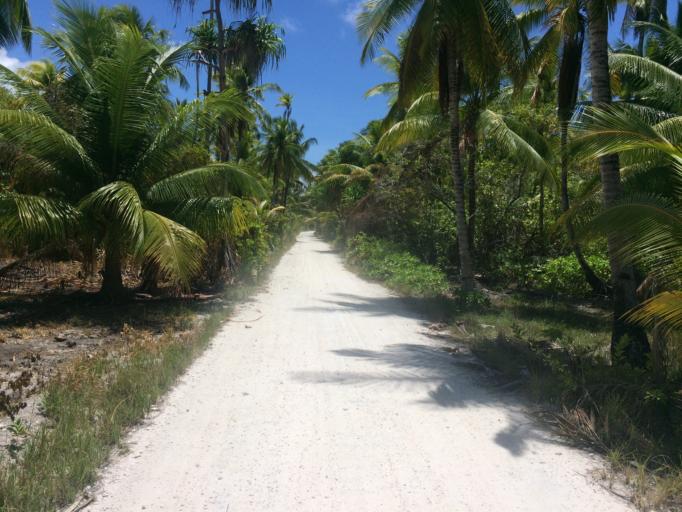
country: KI
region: Gilbert Islands
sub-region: Marakei
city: Rawannawi Village
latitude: 1.7746
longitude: 173.0456
